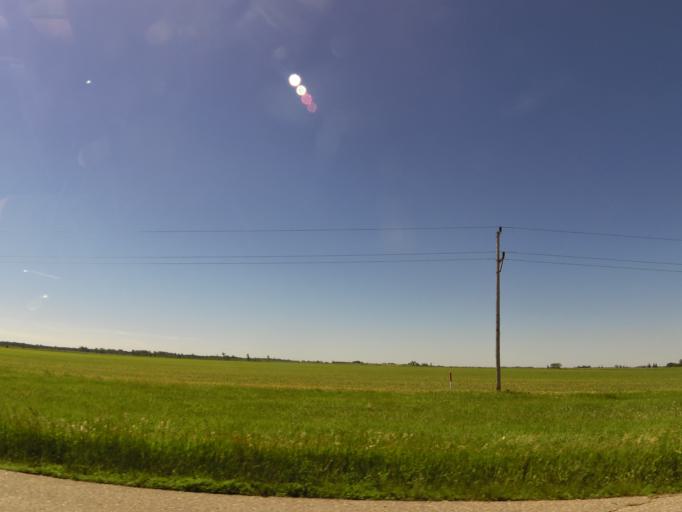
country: US
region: Minnesota
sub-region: Polk County
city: Crookston
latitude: 47.7604
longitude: -96.4463
